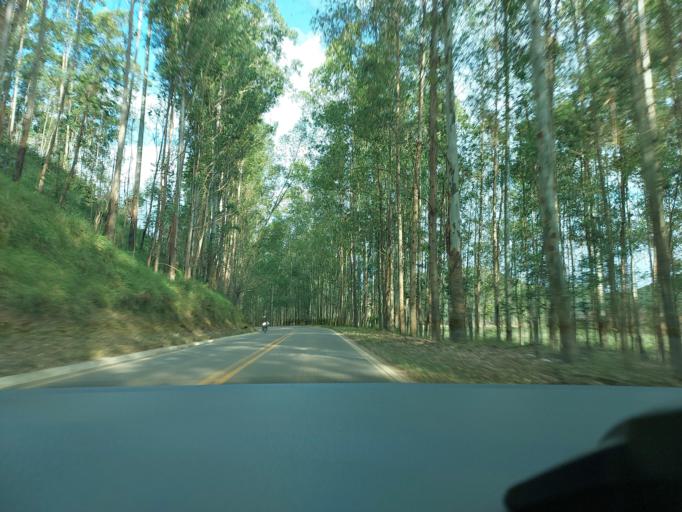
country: BR
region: Minas Gerais
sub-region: Visconde Do Rio Branco
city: Visconde do Rio Branco
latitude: -20.8817
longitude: -42.6639
